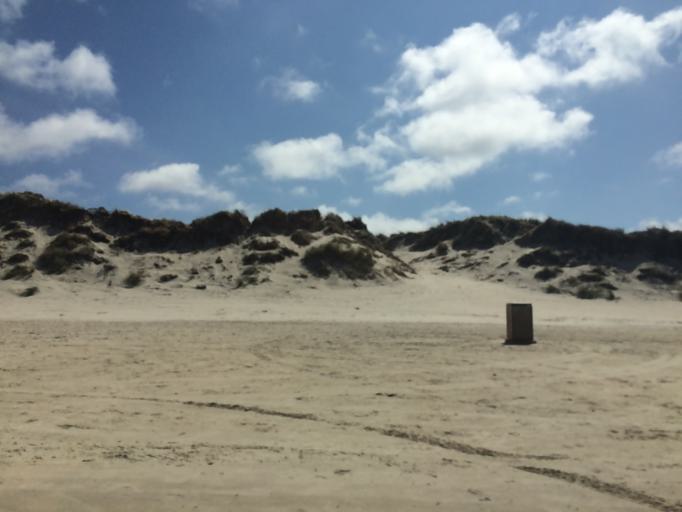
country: DK
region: North Denmark
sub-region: Jammerbugt Kommune
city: Pandrup
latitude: 57.2512
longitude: 9.5746
